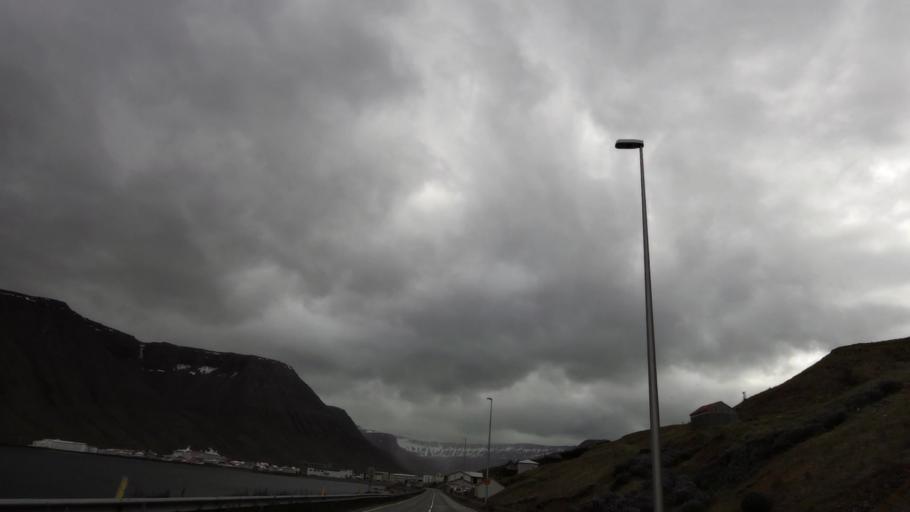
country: IS
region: Westfjords
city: Isafjoerdur
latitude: 66.0838
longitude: -23.1212
